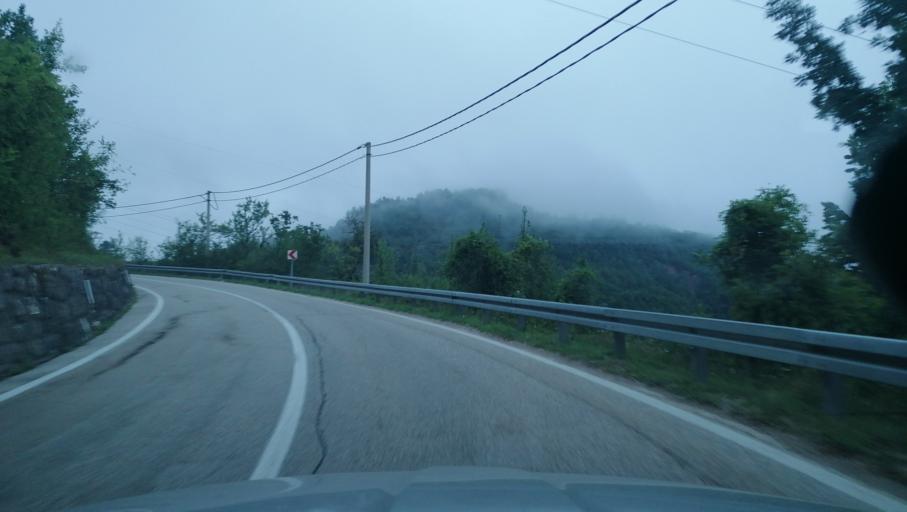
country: BA
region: Federation of Bosnia and Herzegovina
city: Jablanica
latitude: 43.7040
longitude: 17.7176
